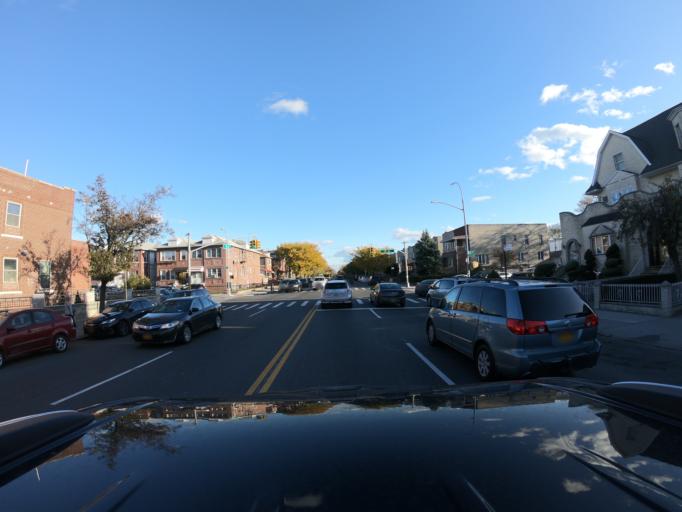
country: US
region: New York
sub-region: Kings County
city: Bensonhurst
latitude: 40.6180
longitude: -73.9884
